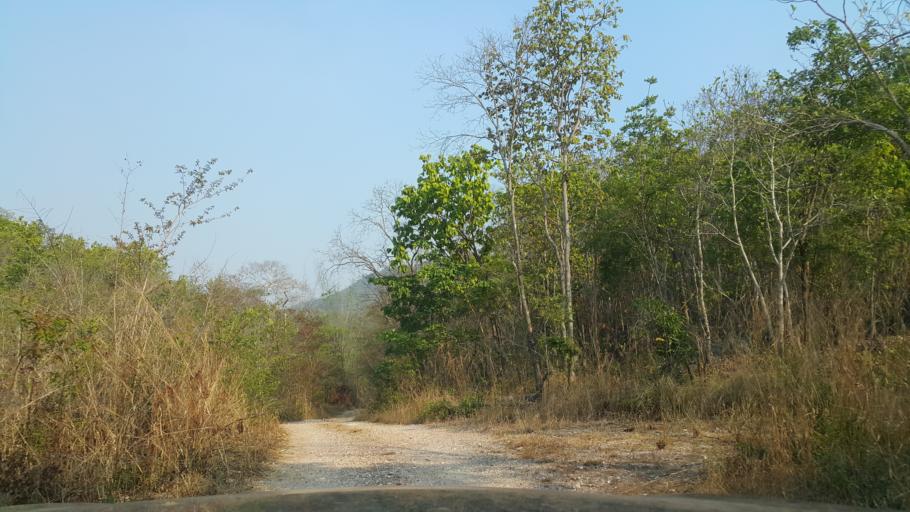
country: TH
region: Sukhothai
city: Thung Saliam
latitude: 17.3322
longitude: 99.4695
